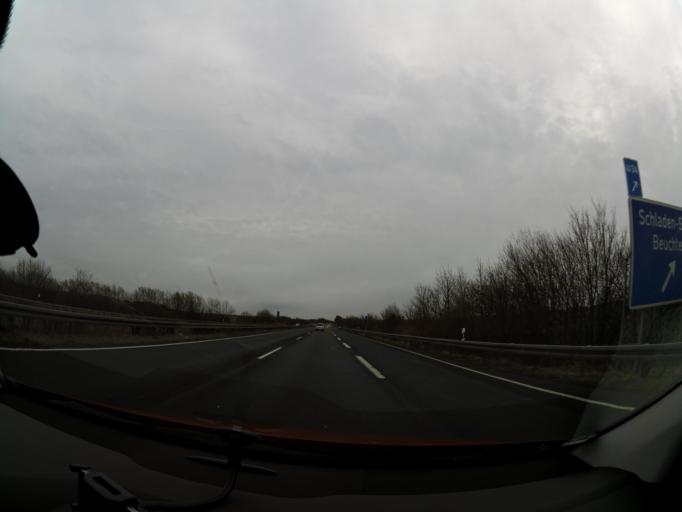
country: DE
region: Lower Saxony
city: Schladen
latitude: 52.0090
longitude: 10.5393
